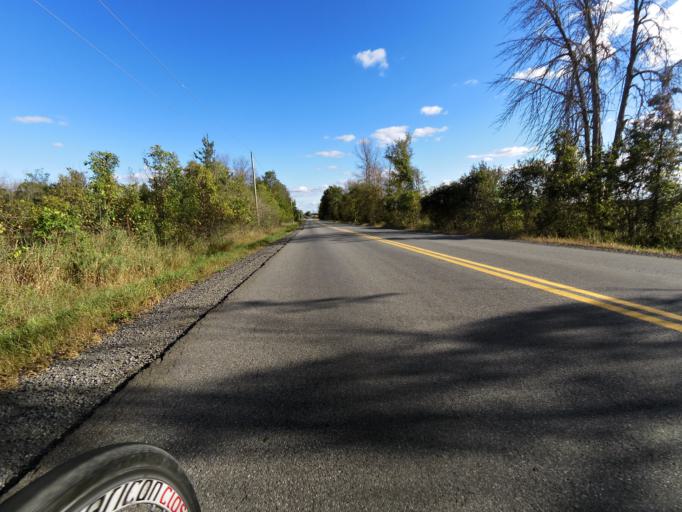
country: CA
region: Ontario
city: Bells Corners
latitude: 45.1403
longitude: -75.7610
